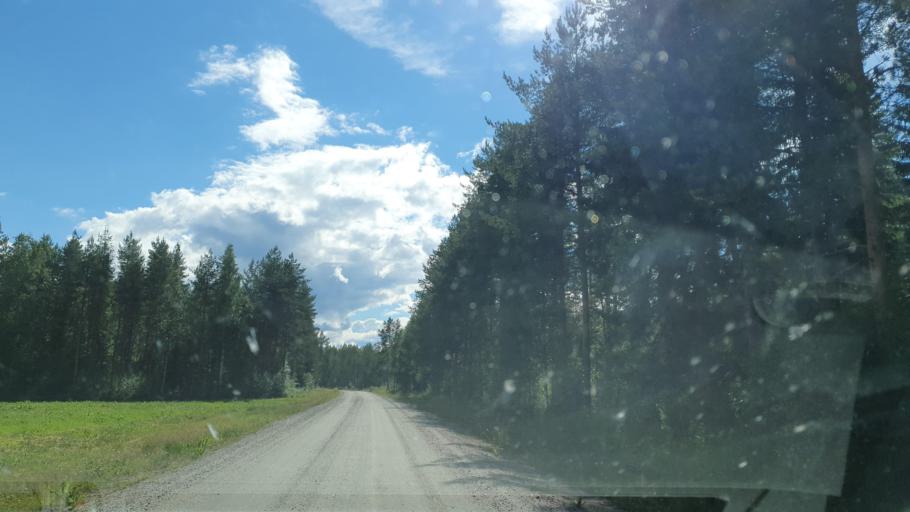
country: FI
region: Kainuu
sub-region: Kehys-Kainuu
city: Kuhmo
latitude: 64.1523
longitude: 29.7930
